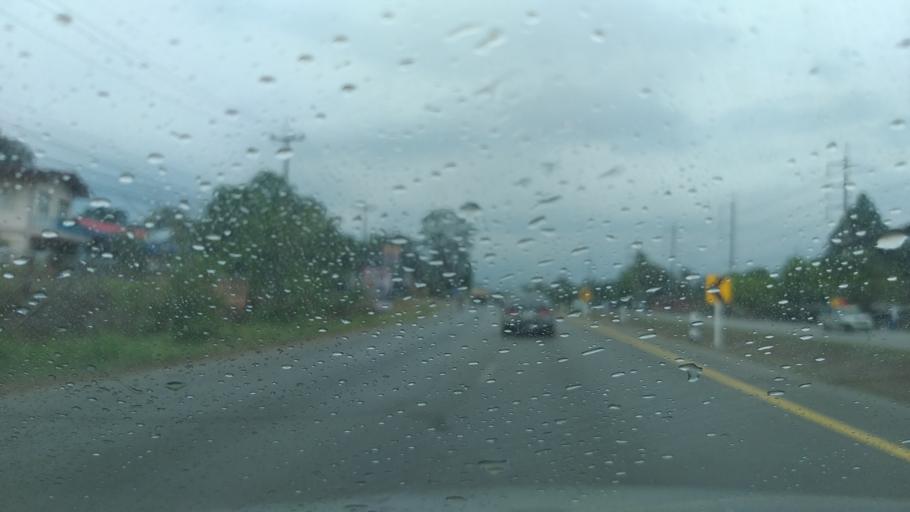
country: TH
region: Chanthaburi
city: Khlung
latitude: 12.4174
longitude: 102.3267
